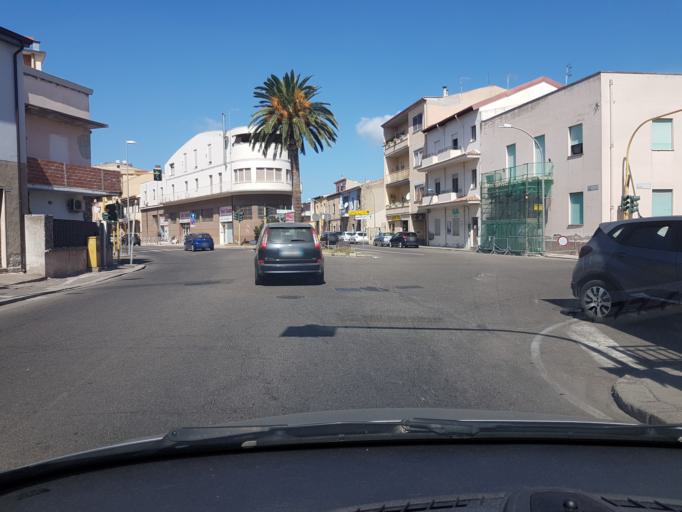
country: IT
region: Sardinia
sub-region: Provincia di Oristano
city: Oristano
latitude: 39.9088
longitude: 8.5958
